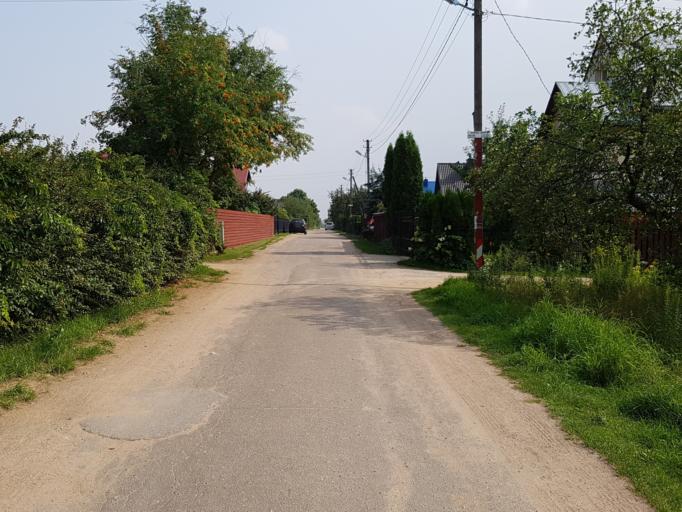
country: LT
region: Vilnius County
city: Rasos
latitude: 54.7924
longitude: 25.3640
